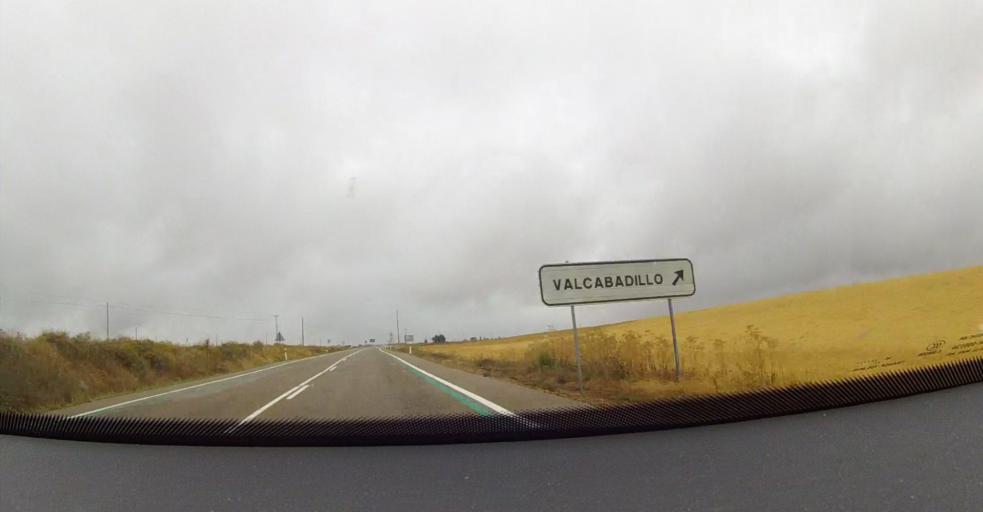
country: ES
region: Castille and Leon
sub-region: Provincia de Palencia
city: Villaluenga de la Vega
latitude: 42.5659
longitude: -4.7541
